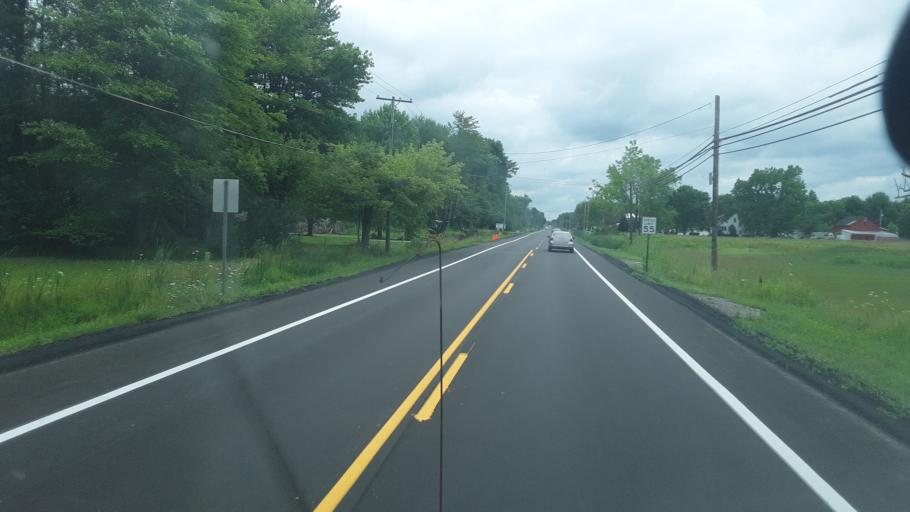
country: US
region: Ohio
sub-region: Trumbull County
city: McKinley Heights
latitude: 41.2435
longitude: -80.6638
